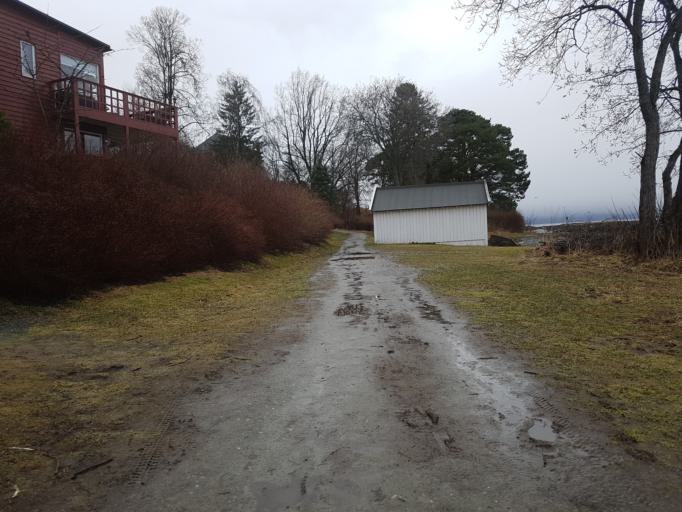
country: NO
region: Sor-Trondelag
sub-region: Trondheim
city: Trondheim
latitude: 63.4369
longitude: 10.4963
